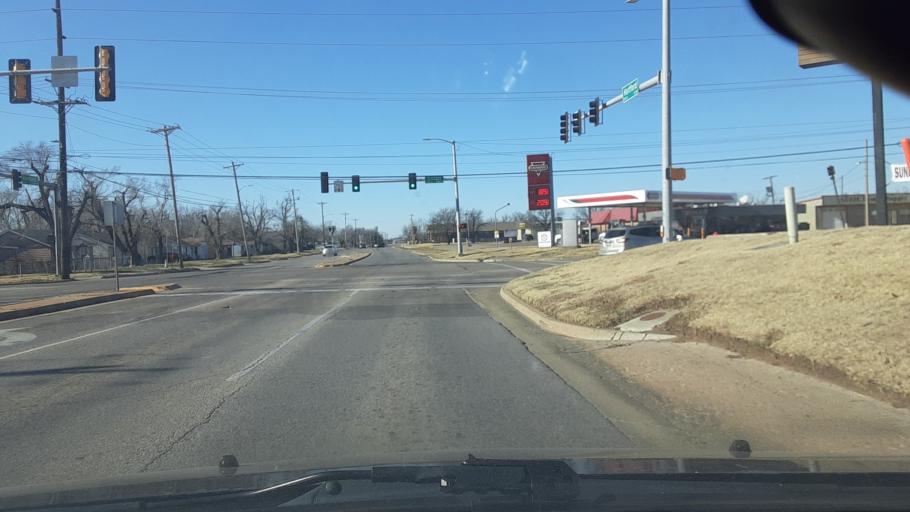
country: US
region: Oklahoma
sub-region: Kay County
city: Ponca City
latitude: 36.7244
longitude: -97.0847
